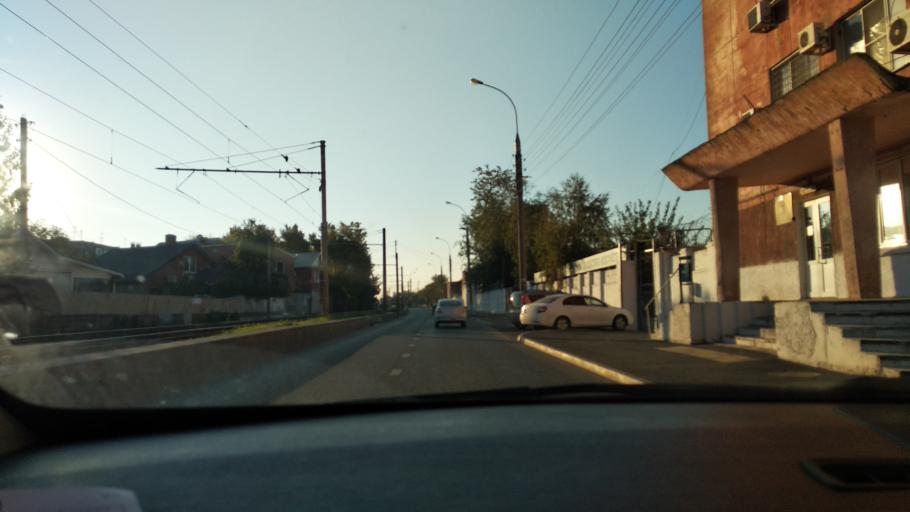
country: RU
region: Krasnodarskiy
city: Krasnodar
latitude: 45.0083
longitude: 39.0150
